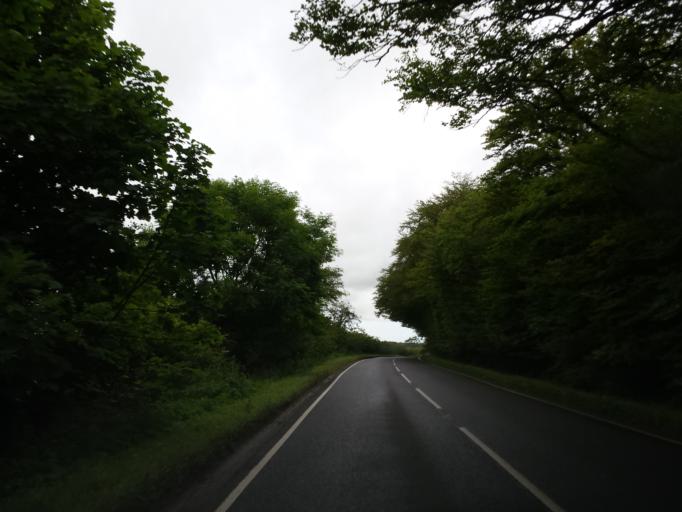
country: GB
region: Scotland
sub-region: Fife
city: Strathkinness
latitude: 56.2768
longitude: -2.8460
